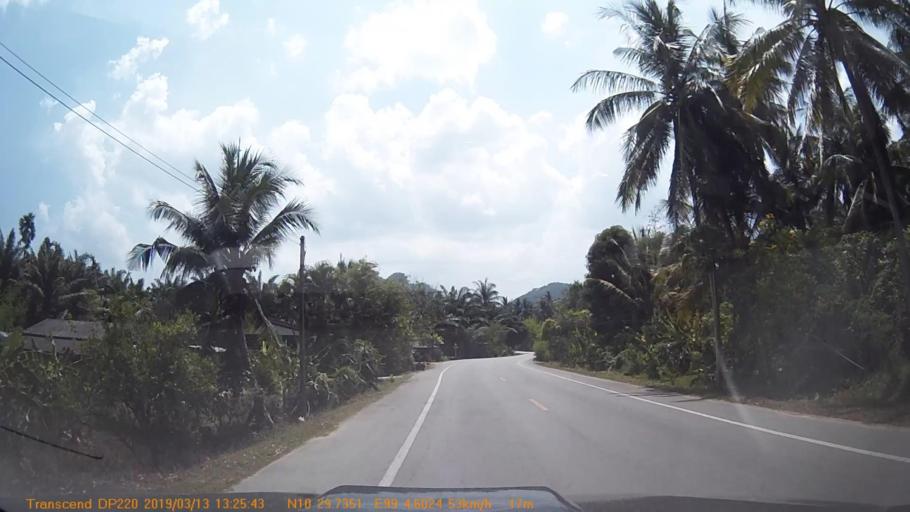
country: TH
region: Chumphon
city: Chumphon
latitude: 10.4984
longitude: 99.0781
